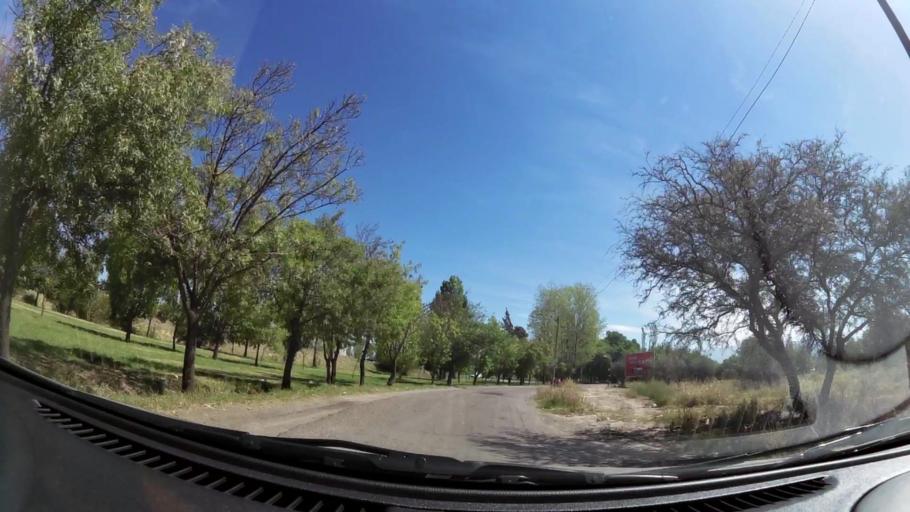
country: AR
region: Mendoza
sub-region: Departamento de Godoy Cruz
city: Godoy Cruz
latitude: -32.9837
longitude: -68.8501
